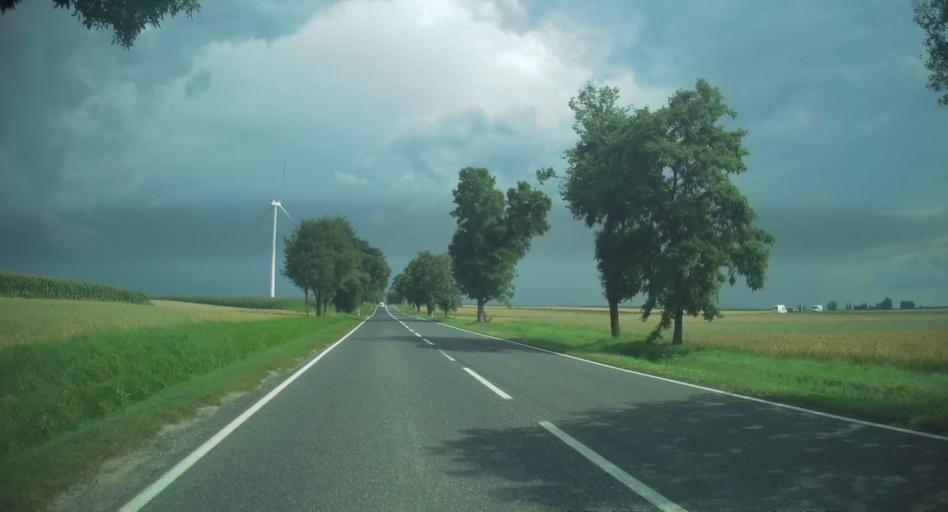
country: PL
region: Lodz Voivodeship
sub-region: Powiat skierniewicki
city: Gluchow
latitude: 51.7921
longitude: 20.0400
